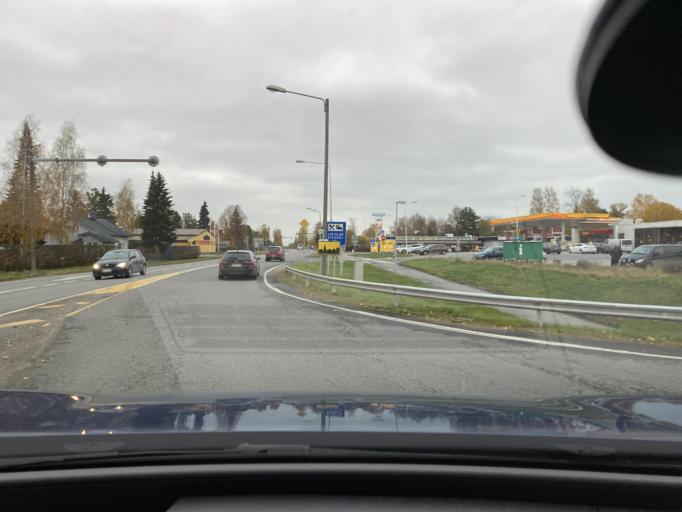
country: FI
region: Varsinais-Suomi
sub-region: Vakka-Suomi
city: Laitila
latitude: 60.8743
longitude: 21.6982
